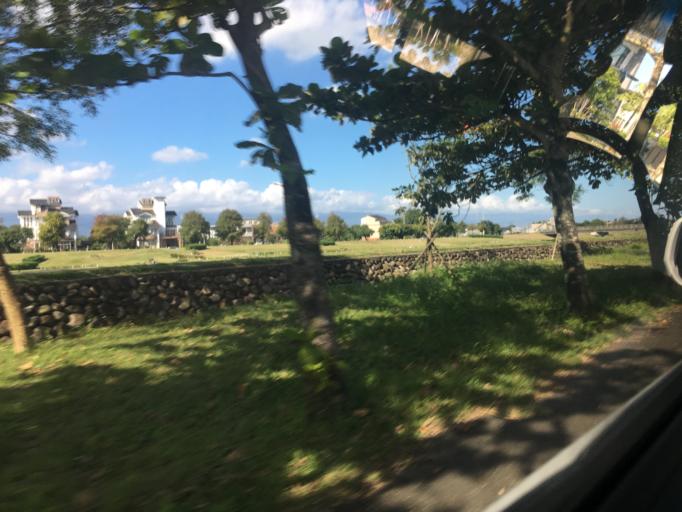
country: TW
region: Taiwan
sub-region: Yilan
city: Yilan
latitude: 24.6947
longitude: 121.7437
